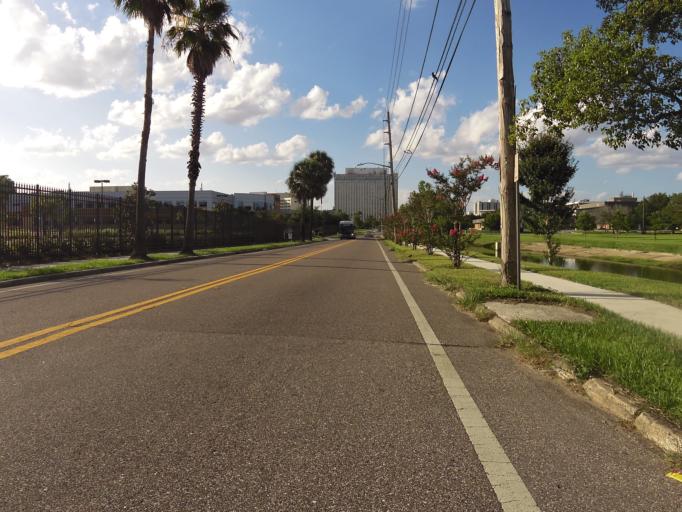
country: US
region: Florida
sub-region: Duval County
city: Jacksonville
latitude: 30.3424
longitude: -81.6630
